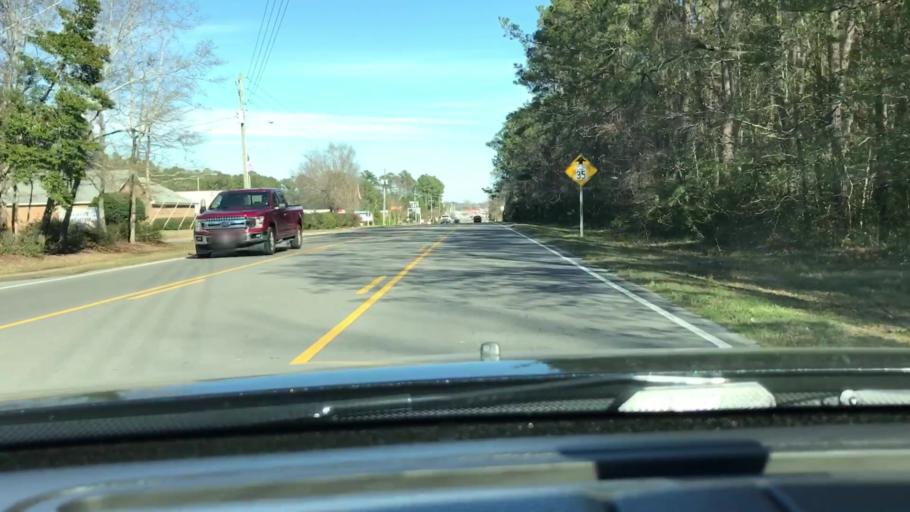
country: US
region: North Carolina
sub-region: Brunswick County
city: Shallotte
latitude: 33.9647
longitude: -78.3960
